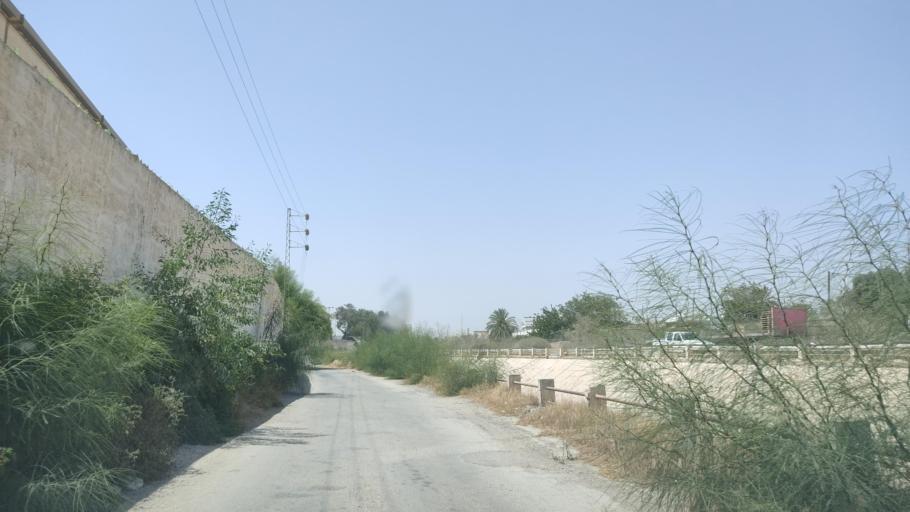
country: TN
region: Safaqis
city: Sfax
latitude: 34.7146
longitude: 10.7310
